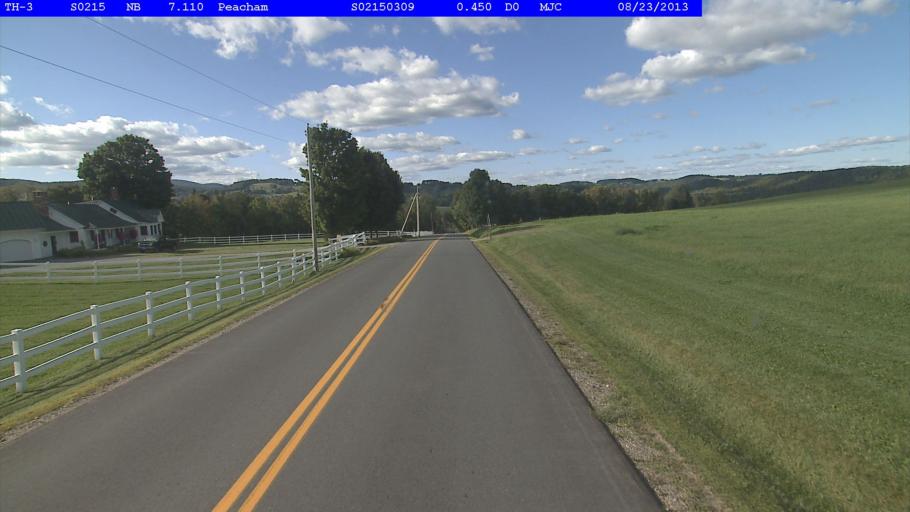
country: US
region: Vermont
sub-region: Caledonia County
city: Saint Johnsbury
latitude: 44.3043
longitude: -72.1646
